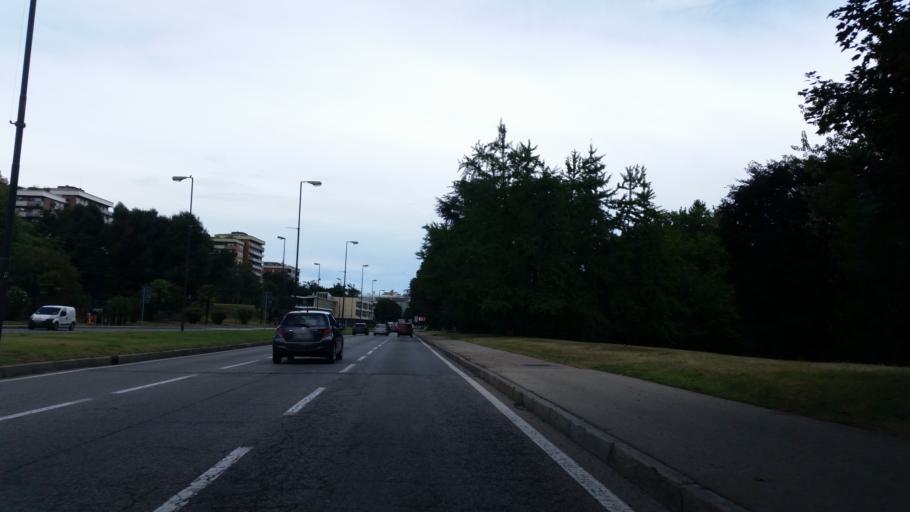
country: IT
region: Piedmont
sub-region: Provincia di Torino
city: Moncalieri
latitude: 45.0268
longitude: 7.6720
